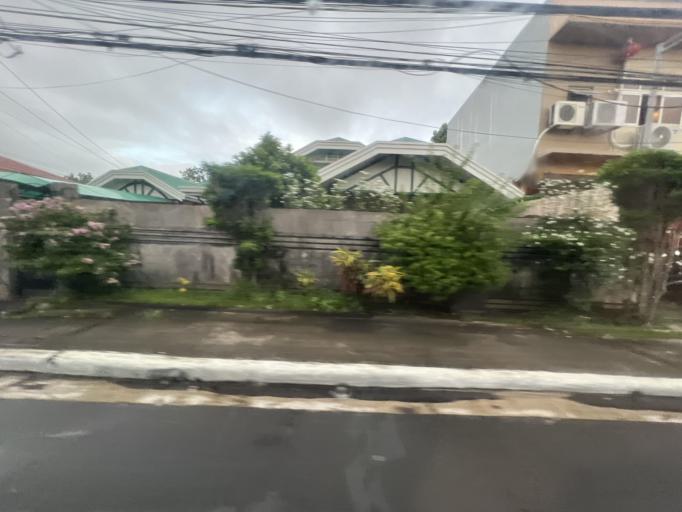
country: PH
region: Bicol
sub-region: Province of Albay
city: Sagpon
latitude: 13.1537
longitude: 123.7345
